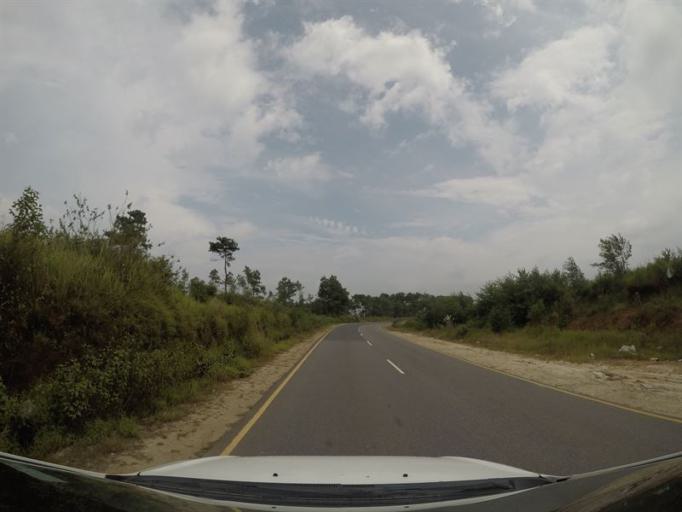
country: IN
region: Meghalaya
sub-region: East Khasi Hills
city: Shillong
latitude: 25.4905
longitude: 92.1882
